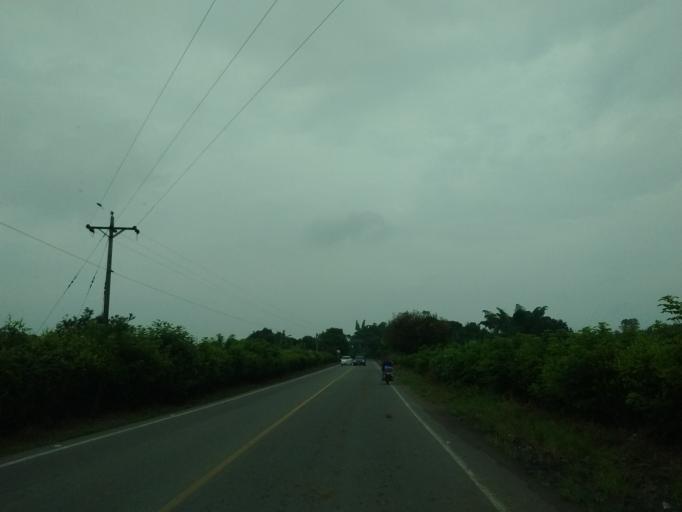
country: CO
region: Cauca
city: Padilla
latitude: 3.2287
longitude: -76.3222
